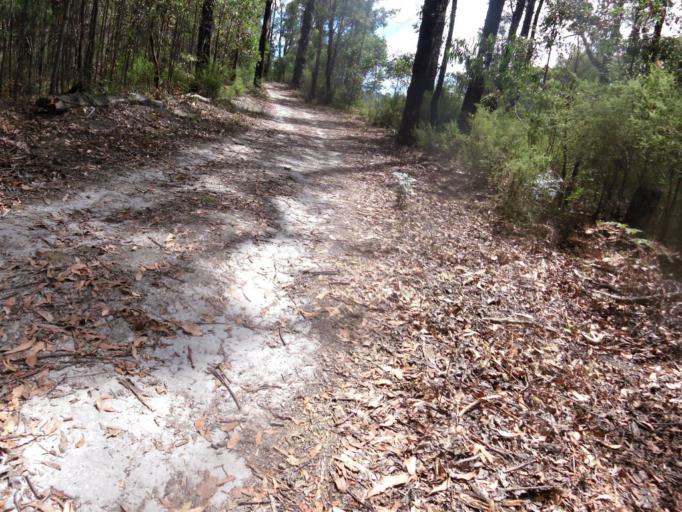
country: AU
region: Victoria
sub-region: Nillumbik
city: Saint Andrews
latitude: -37.5439
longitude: 145.3415
